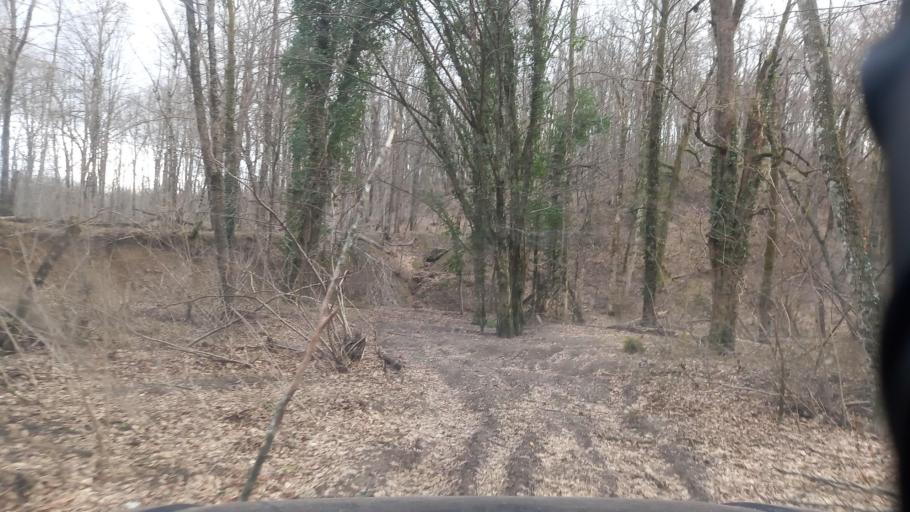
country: RU
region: Krasnodarskiy
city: Dzhubga
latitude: 44.4854
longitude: 38.7830
